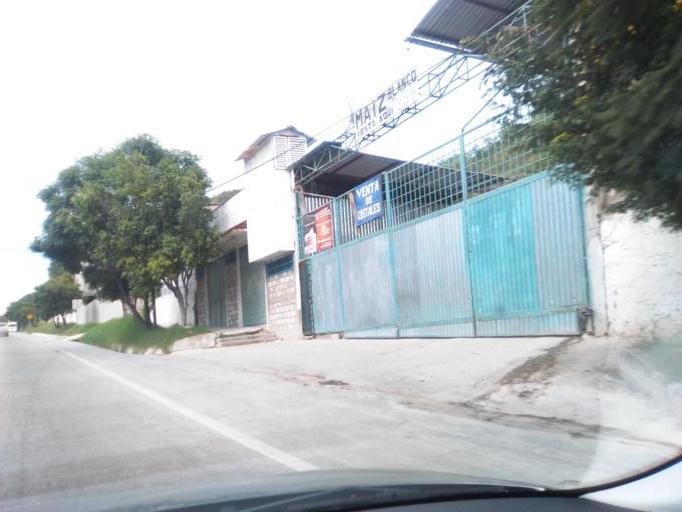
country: MX
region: Guerrero
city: Chilpancingo de los Bravos
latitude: 17.5901
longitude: -99.5172
